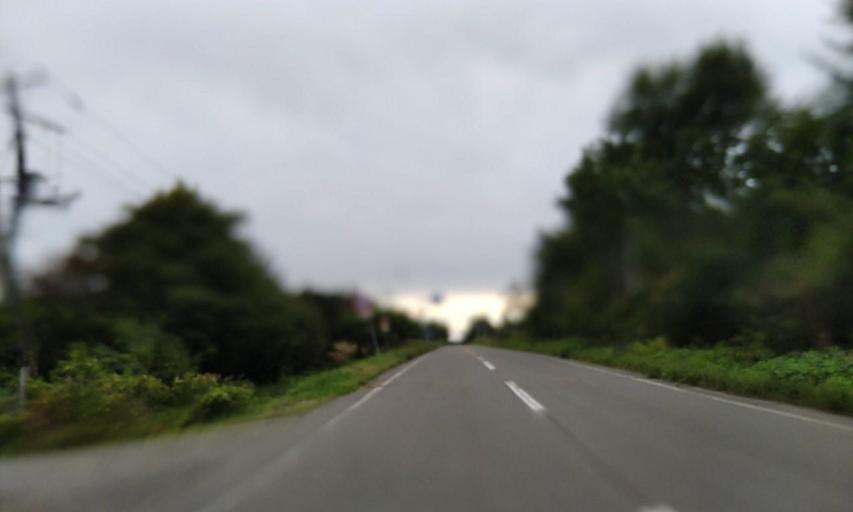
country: JP
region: Hokkaido
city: Obihiro
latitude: 42.6632
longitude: 143.0720
